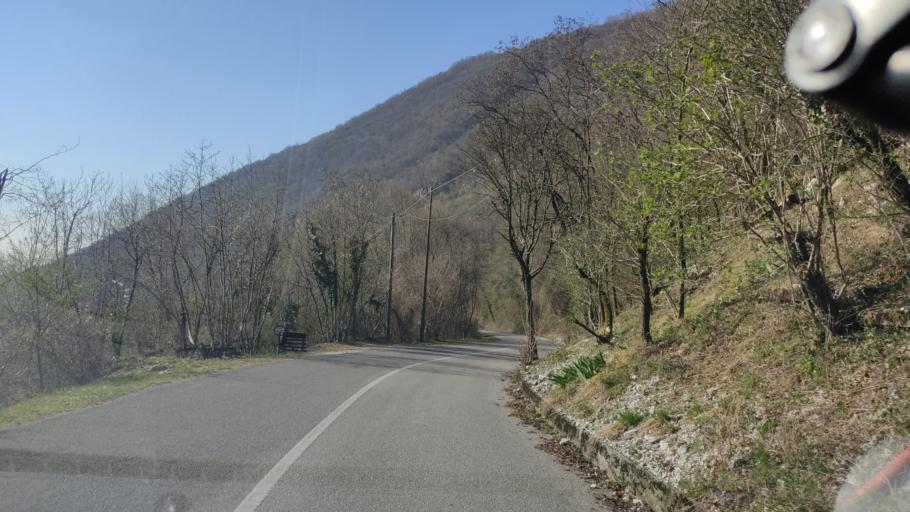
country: IT
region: Friuli Venezia Giulia
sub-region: Provincia di Pordenone
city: Polcenigo
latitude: 46.0699
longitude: 12.5105
